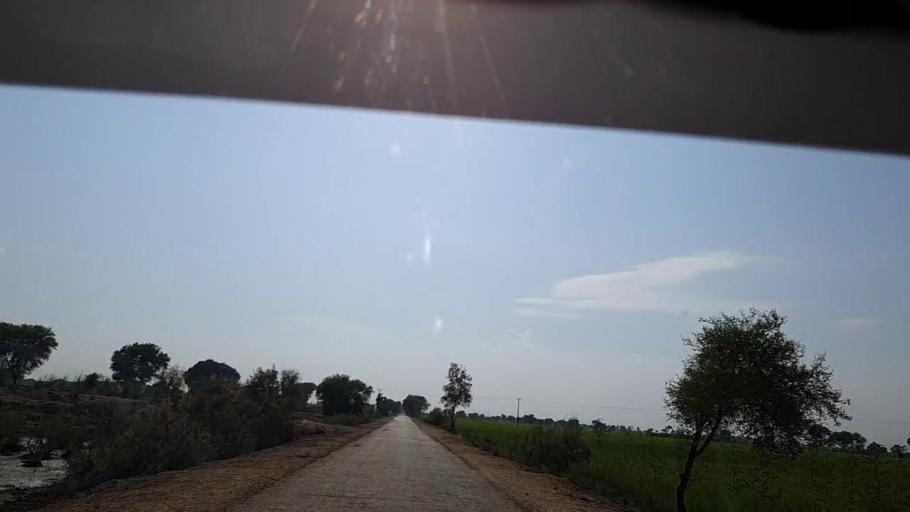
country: PK
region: Sindh
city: Shikarpur
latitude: 28.0829
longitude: 68.6543
